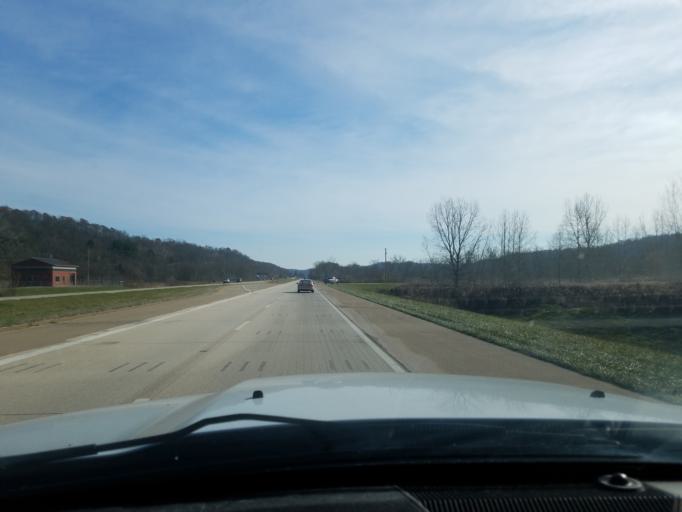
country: US
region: Ohio
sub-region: Athens County
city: Athens
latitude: 39.3309
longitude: -82.0046
